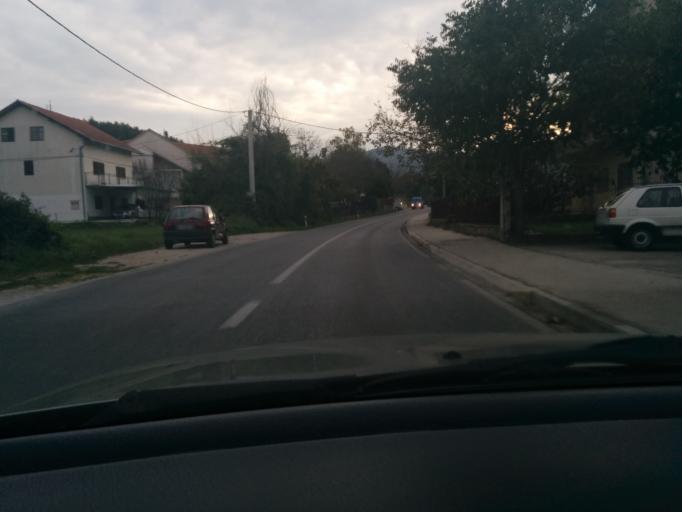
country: HR
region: Splitsko-Dalmatinska
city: Sinj
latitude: 43.7086
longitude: 16.6568
